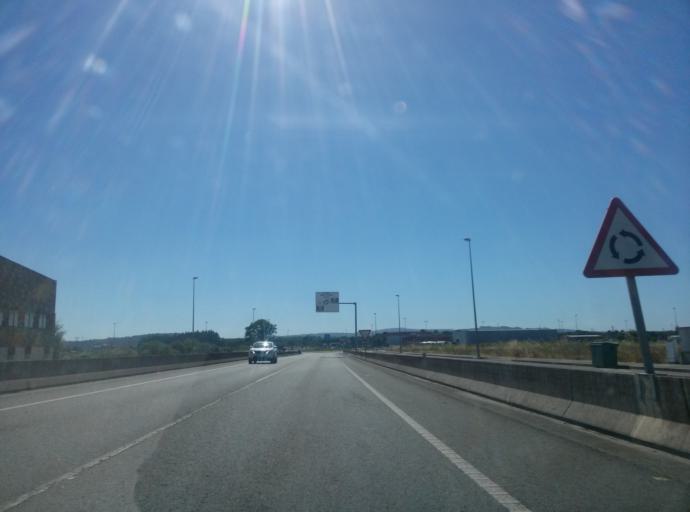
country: ES
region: Galicia
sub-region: Provincia de Lugo
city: Outeiro de Rei
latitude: 43.1083
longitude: -7.5977
